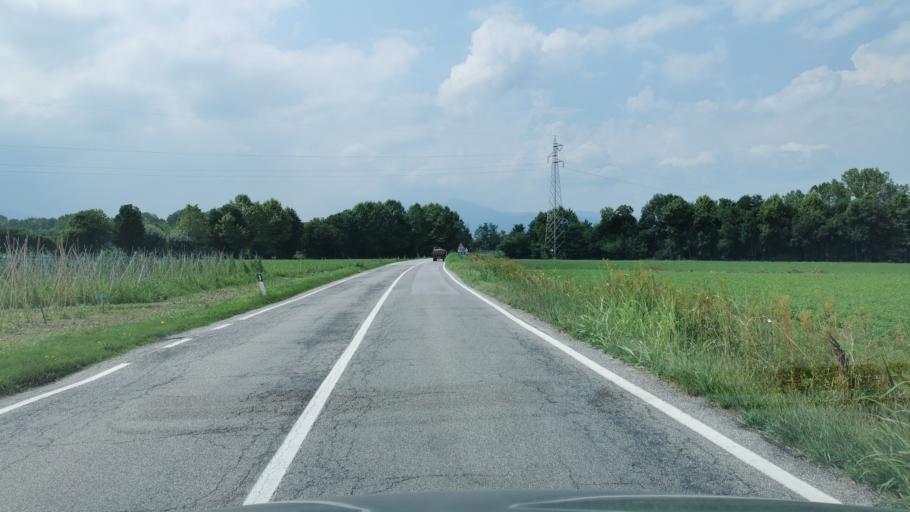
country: IT
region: Piedmont
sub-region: Provincia di Cuneo
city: Roata Rossi
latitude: 44.4344
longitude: 7.5013
